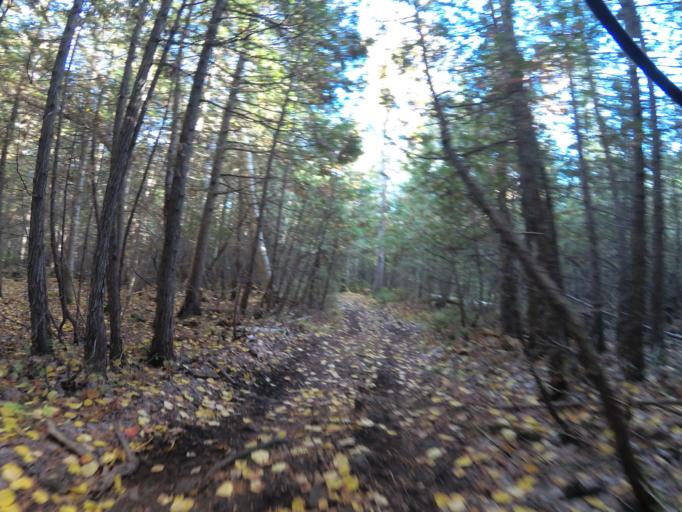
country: CA
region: Ontario
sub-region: Lanark County
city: Smiths Falls
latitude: 45.0329
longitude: -75.8048
